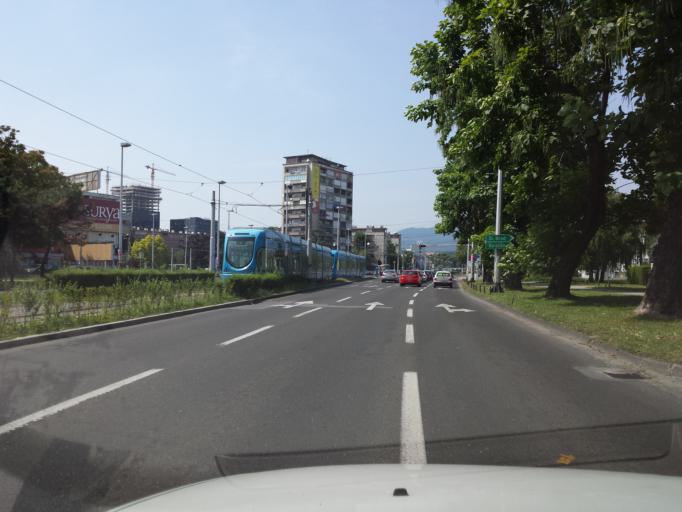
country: HR
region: Grad Zagreb
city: Novi Zagreb
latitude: 45.8000
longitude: 15.9963
